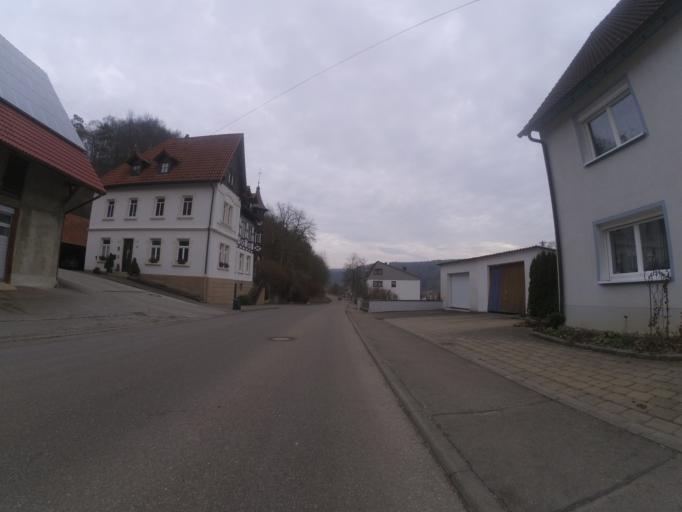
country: DE
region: Baden-Wuerttemberg
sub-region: Tuebingen Region
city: Mehrstetten
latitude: 48.3726
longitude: 9.6398
